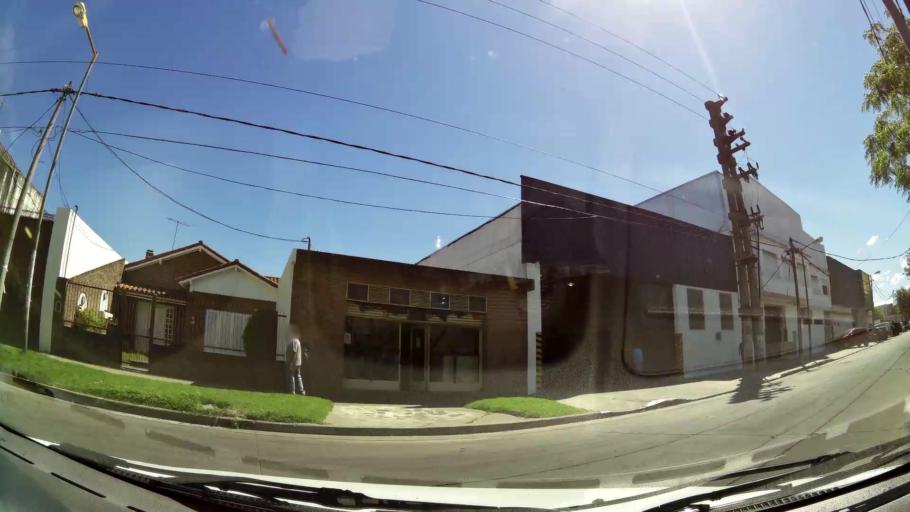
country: AR
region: Buenos Aires
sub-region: Partido de General San Martin
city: General San Martin
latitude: -34.5353
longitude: -58.5630
